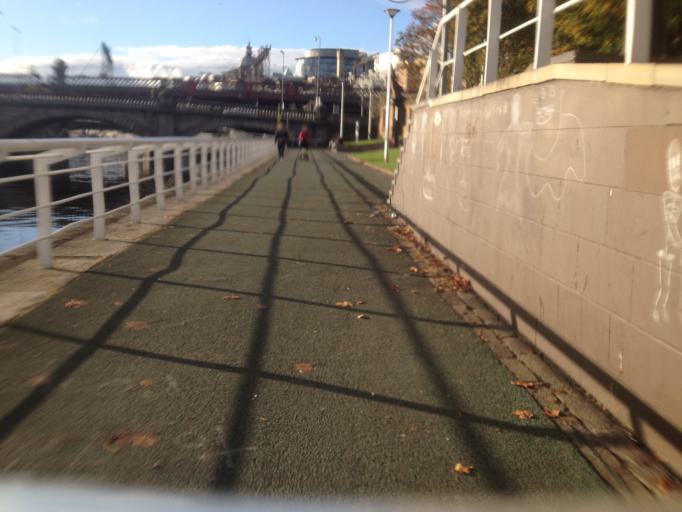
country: GB
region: Scotland
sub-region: Glasgow City
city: Glasgow
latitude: 55.8558
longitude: -4.2562
